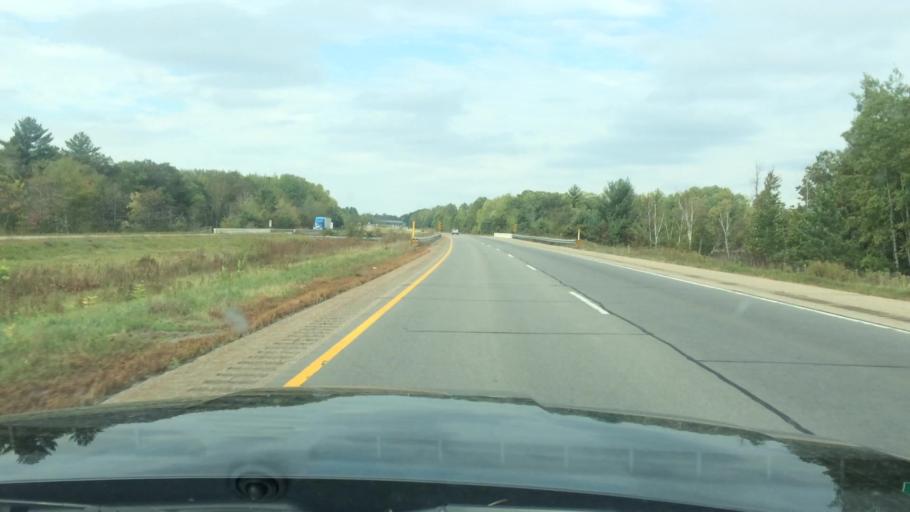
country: US
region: Wisconsin
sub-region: Marathon County
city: Mosinee
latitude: 44.7172
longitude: -89.6631
